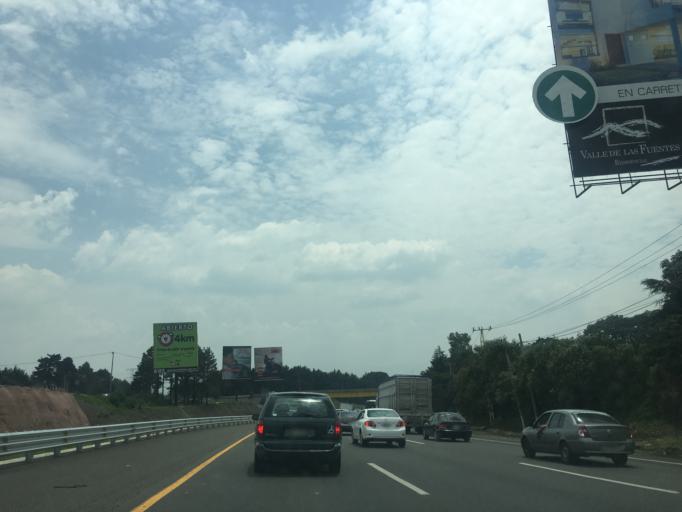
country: MX
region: Morelos
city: San Jeronimo Acazulco
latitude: 19.2931
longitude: -99.4249
